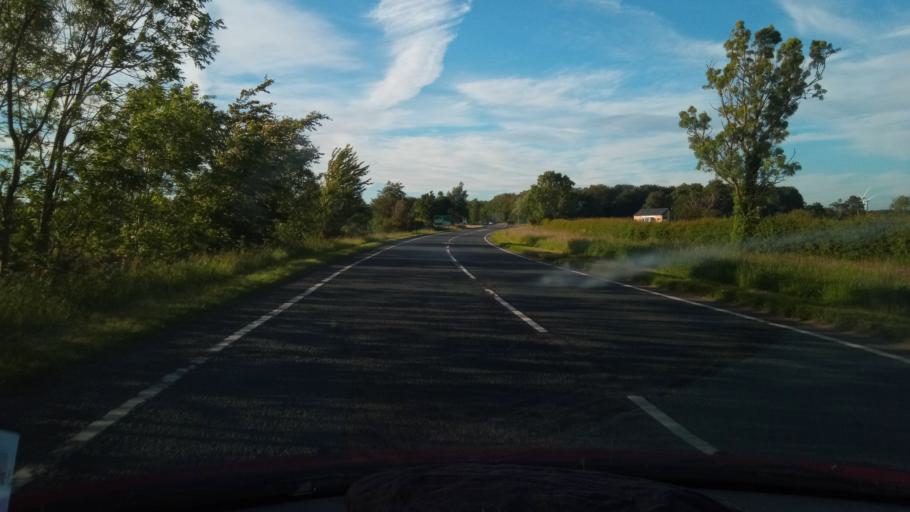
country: GB
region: England
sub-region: Cumbria
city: Carlisle
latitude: 54.9818
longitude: -2.9529
